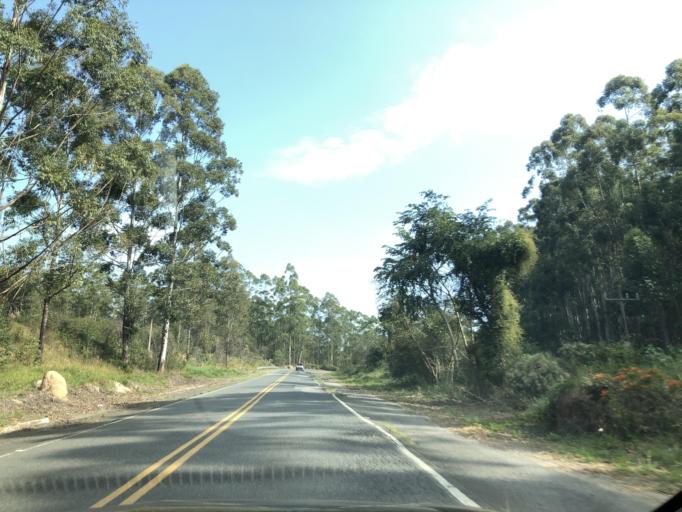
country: BR
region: Sao Paulo
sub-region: Pilar Do Sul
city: Pilar do Sul
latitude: -23.8159
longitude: -47.6480
